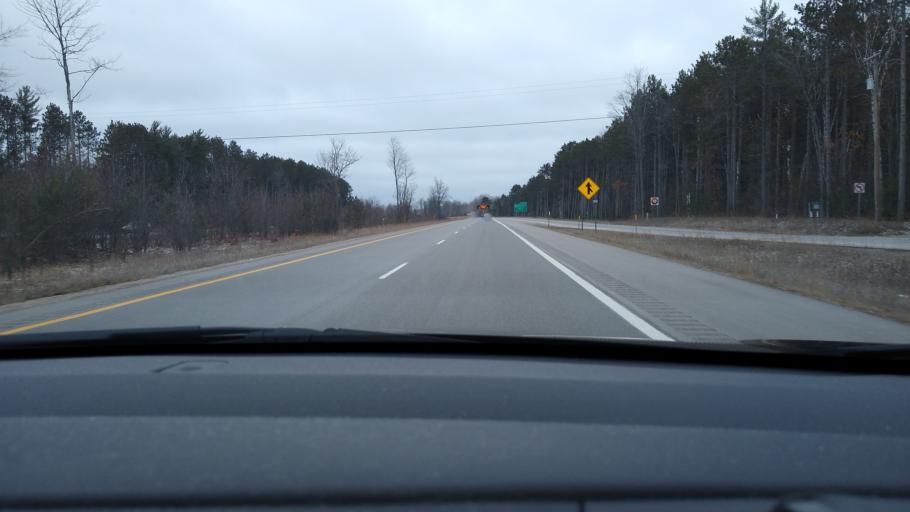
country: US
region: Michigan
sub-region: Otsego County
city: Gaylord
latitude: 44.9686
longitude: -84.6713
